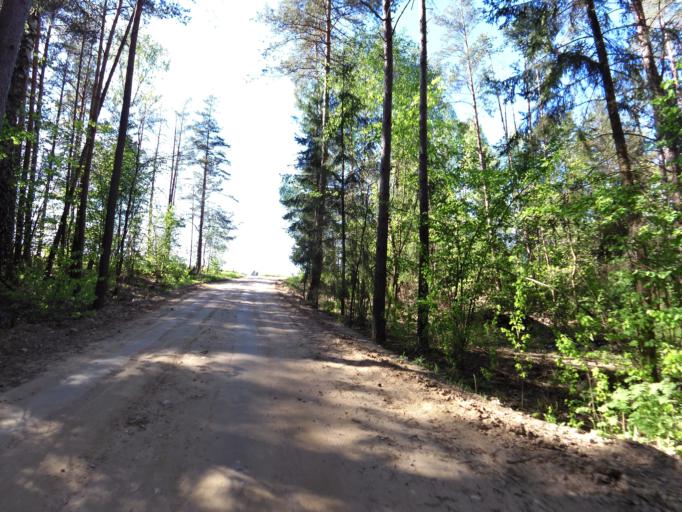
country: LT
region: Vilnius County
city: Pilaite
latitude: 54.6888
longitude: 25.1627
